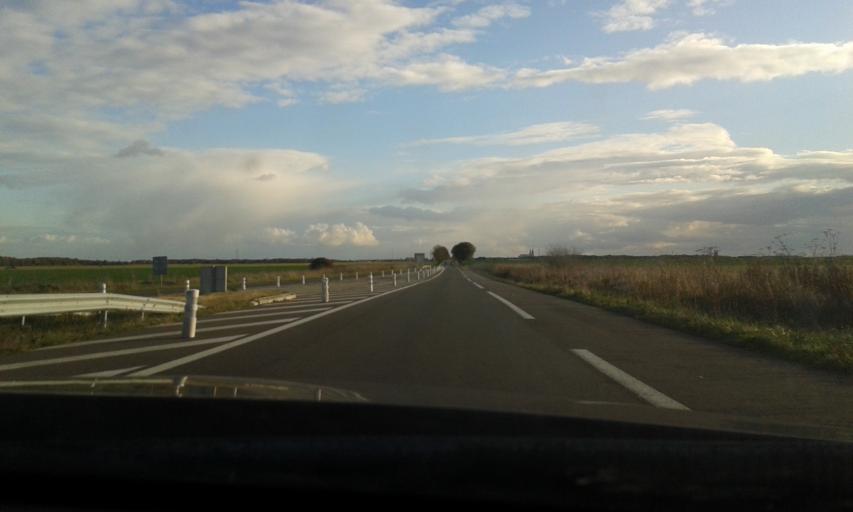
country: FR
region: Centre
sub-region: Departement d'Eure-et-Loir
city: Leves
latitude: 48.5015
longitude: 1.4664
